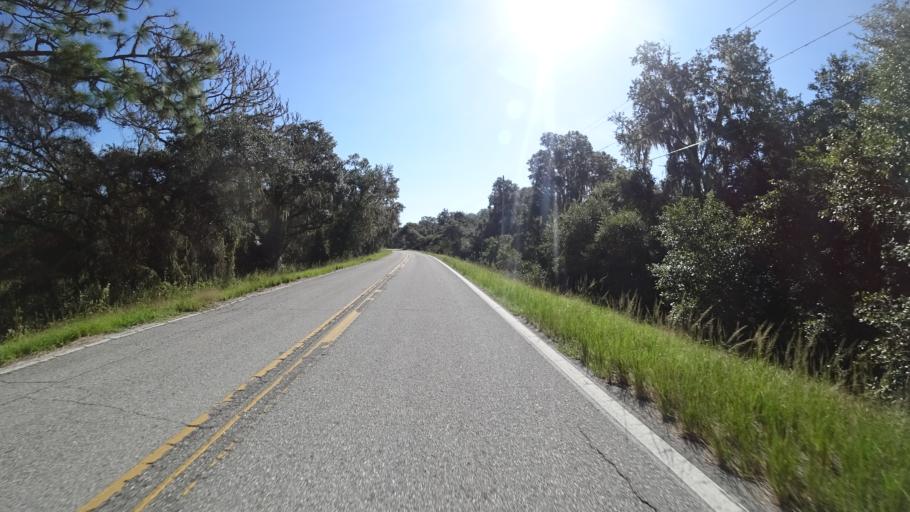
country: US
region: Florida
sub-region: Hillsborough County
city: Wimauma
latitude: 27.6626
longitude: -82.3004
